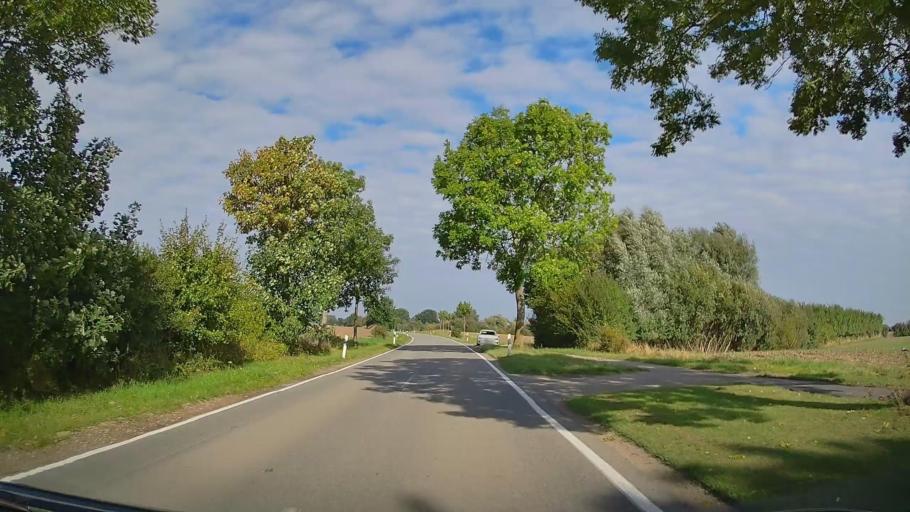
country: DE
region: Schleswig-Holstein
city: Oldenburg in Holstein
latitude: 54.3308
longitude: 10.8928
